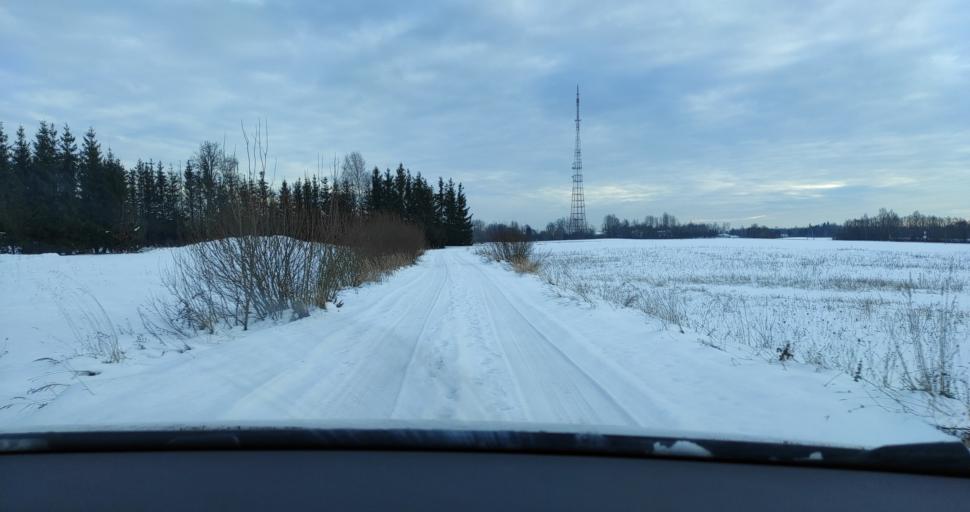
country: LV
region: Kuldigas Rajons
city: Kuldiga
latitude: 56.9423
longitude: 22.0067
